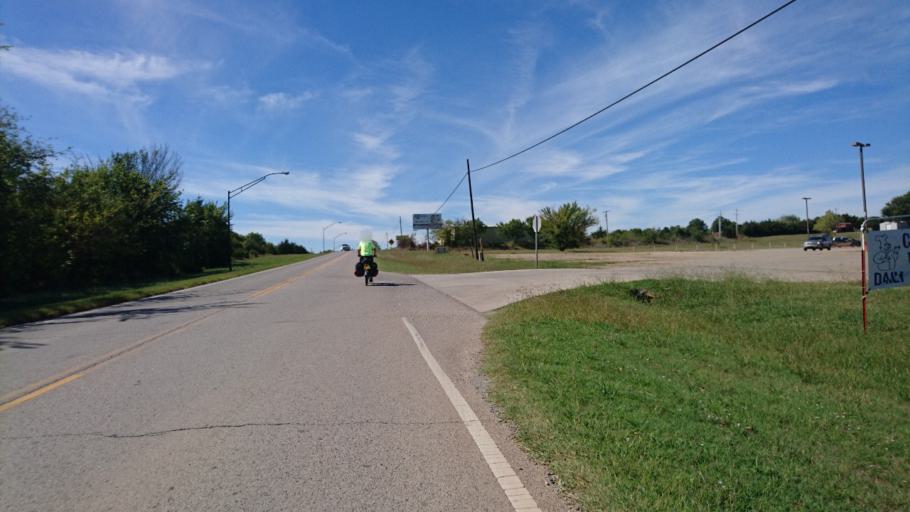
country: US
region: Oklahoma
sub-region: Lincoln County
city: Stroud
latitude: 35.7504
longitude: -96.6694
